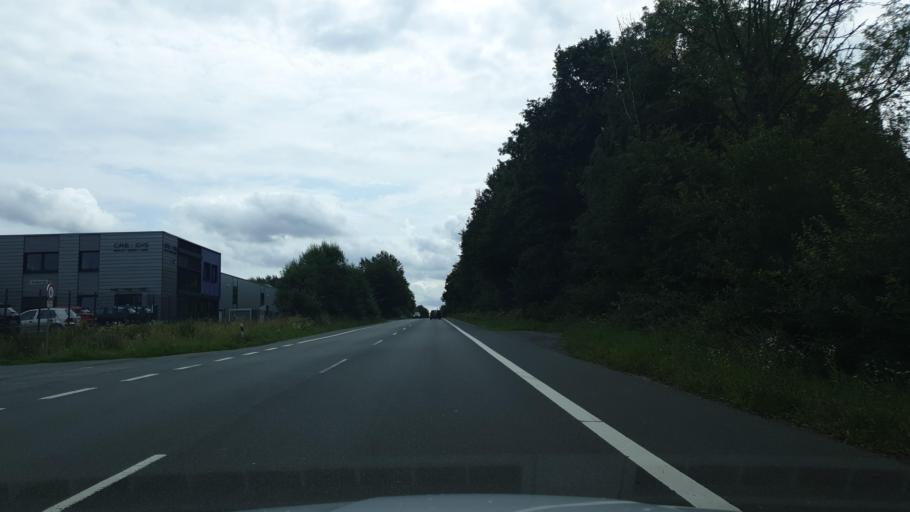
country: DE
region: Lower Saxony
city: Georgsmarienhutte
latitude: 52.2194
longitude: 8.1035
